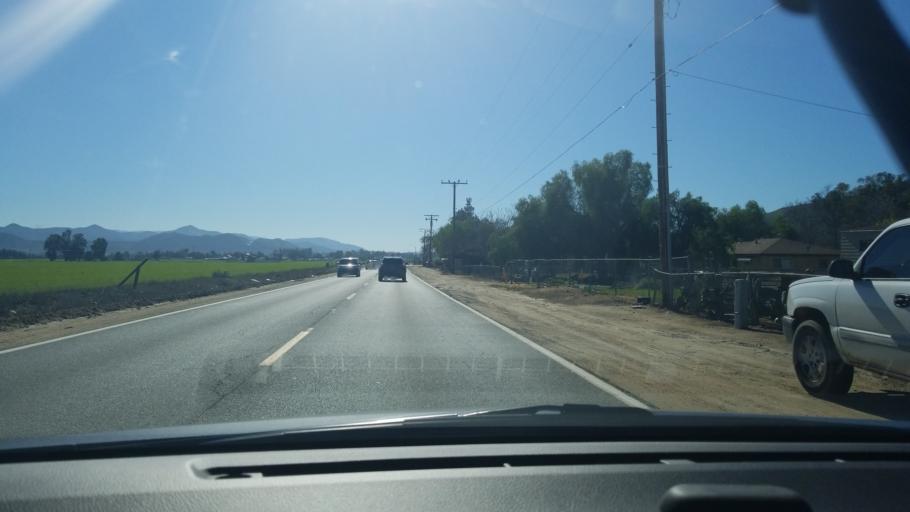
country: US
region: California
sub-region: Riverside County
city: Green Acres
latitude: 33.7344
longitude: -117.0764
